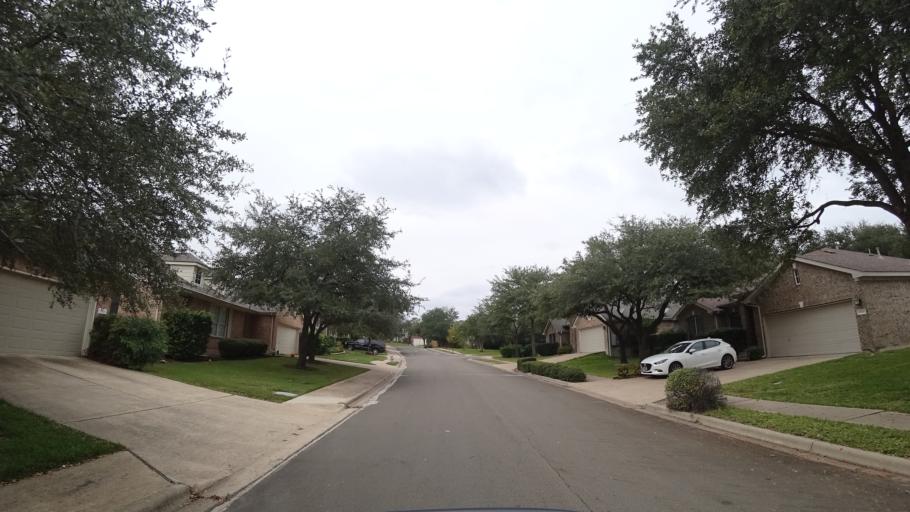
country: US
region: Texas
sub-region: Travis County
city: Shady Hollow
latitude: 30.2129
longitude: -97.8887
